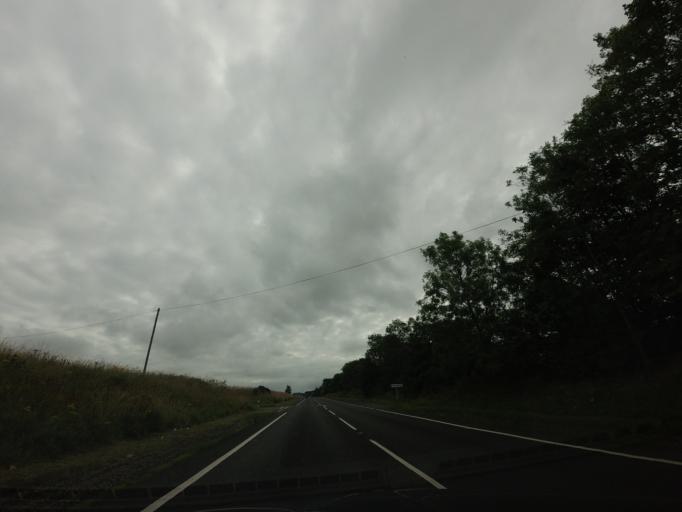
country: GB
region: Scotland
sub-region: Dumfries and Galloway
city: Gretna
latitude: 54.9951
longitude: -3.0951
